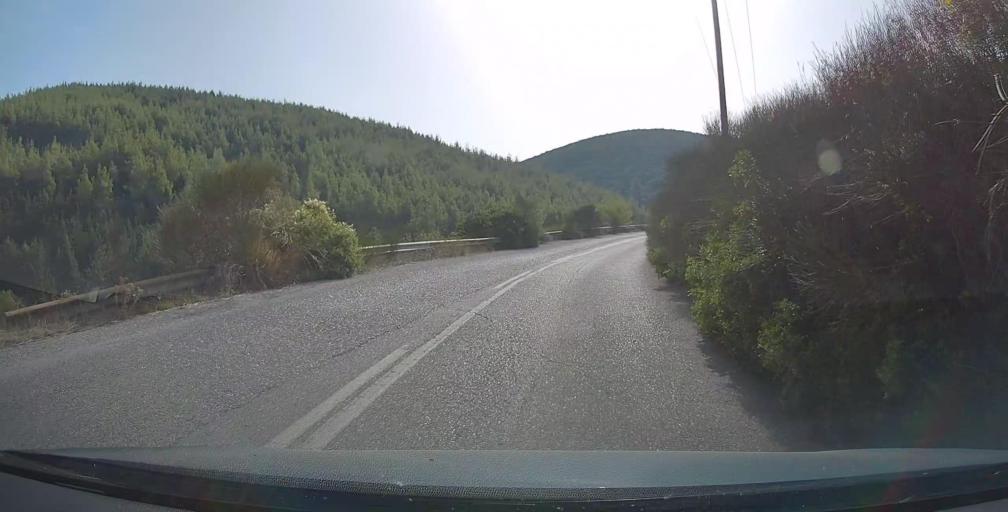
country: GR
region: Central Macedonia
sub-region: Nomos Chalkidikis
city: Sykia
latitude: 39.9618
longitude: 23.9398
